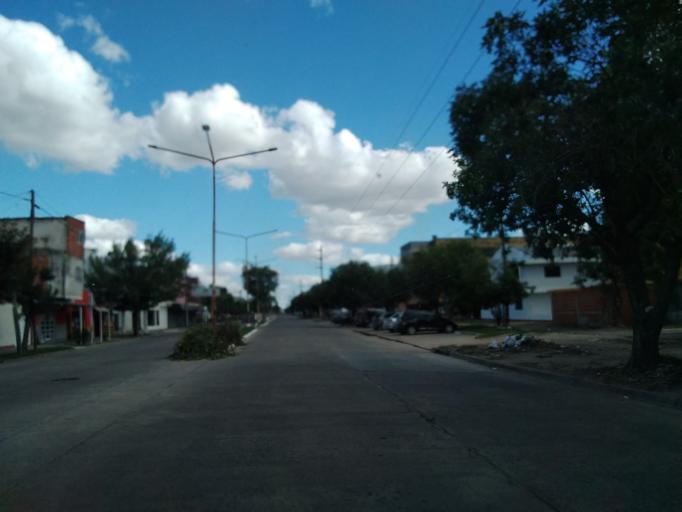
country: AR
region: Corrientes
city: Corrientes
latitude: -27.4934
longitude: -58.8264
